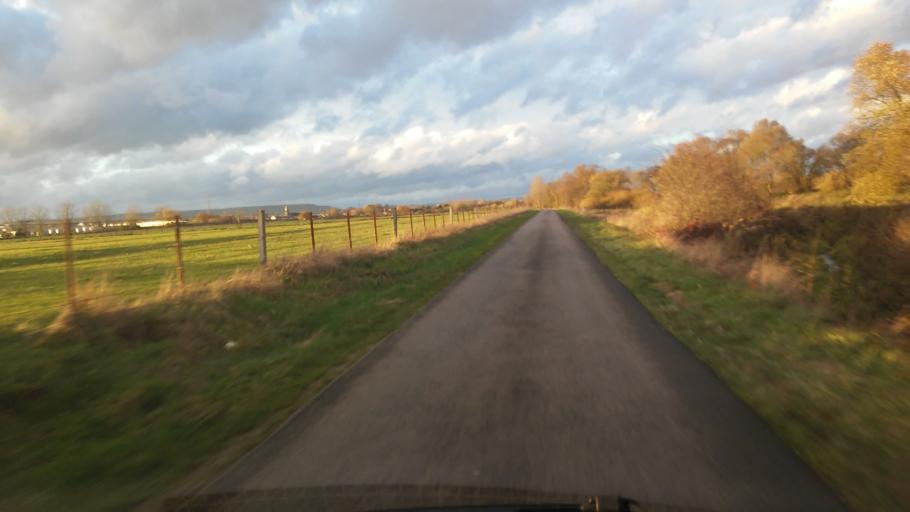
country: FR
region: Lorraine
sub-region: Departement de la Moselle
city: Ay-sur-Moselle
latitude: 49.2261
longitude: 6.1917
